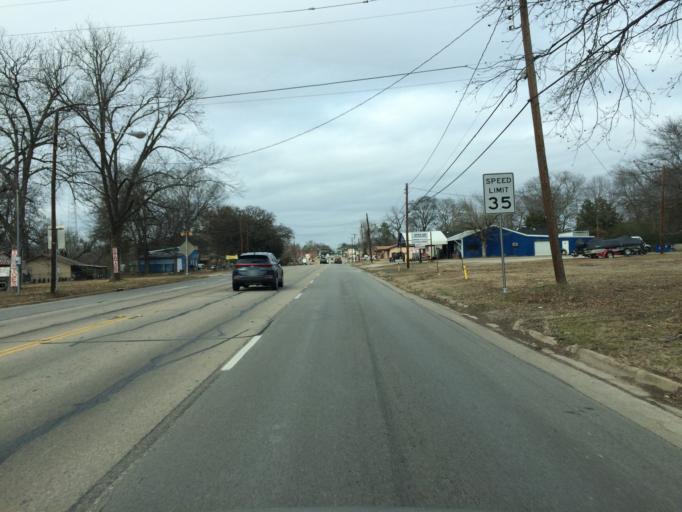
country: US
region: Texas
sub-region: Wood County
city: Mineola
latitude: 32.6571
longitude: -95.4900
